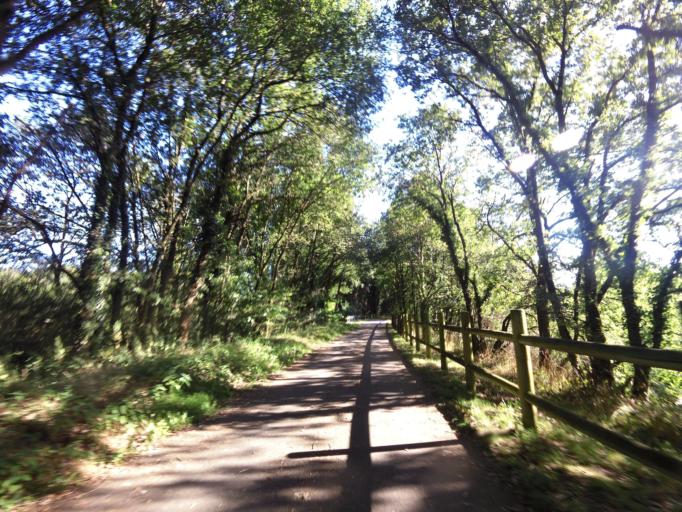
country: FR
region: Brittany
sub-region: Departement du Morbihan
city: Guillac
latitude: 47.9130
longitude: -2.4298
